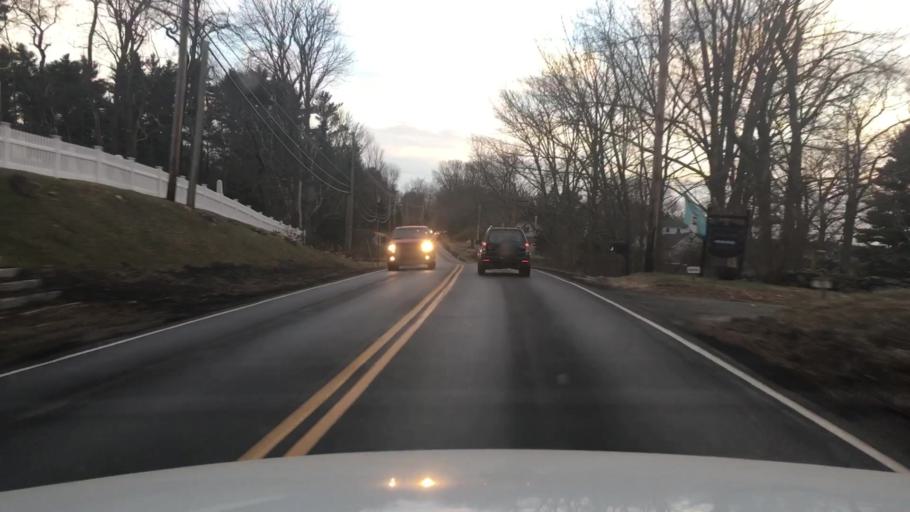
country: US
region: Maine
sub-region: Lincoln County
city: Damariscotta
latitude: 44.0145
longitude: -69.5311
